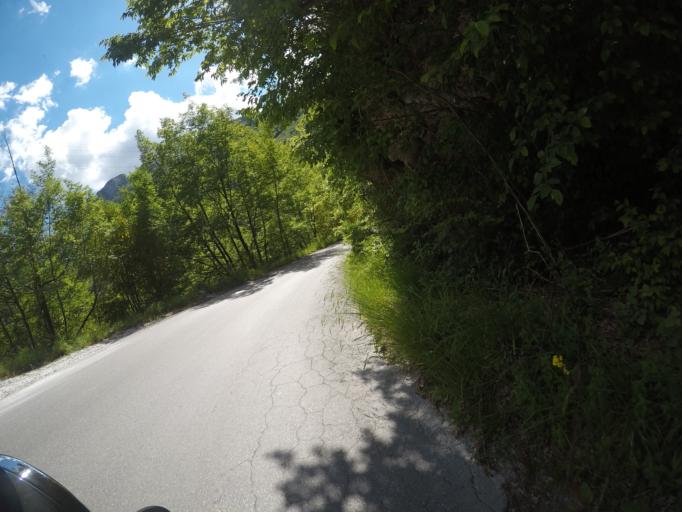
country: IT
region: Tuscany
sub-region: Provincia di Lucca
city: Minucciano
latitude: 44.1518
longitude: 10.1982
